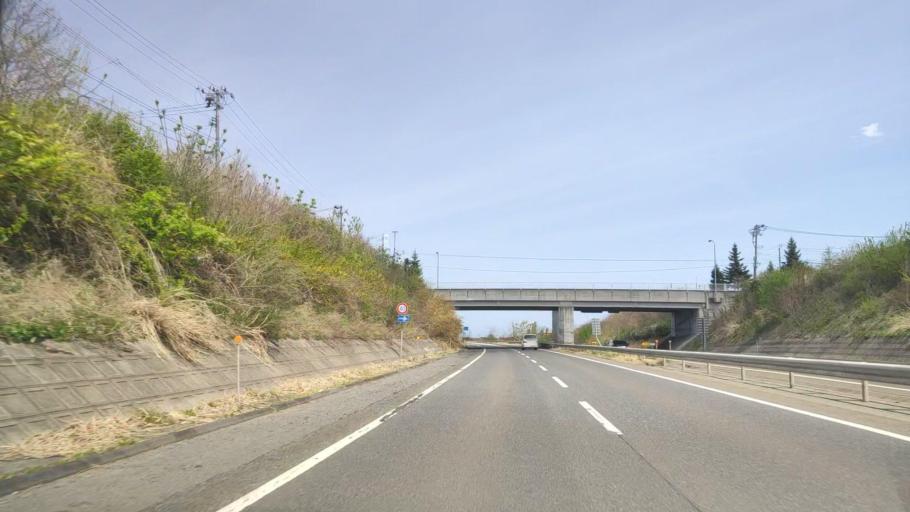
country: JP
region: Aomori
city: Hachinohe
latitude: 40.4897
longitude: 141.4641
